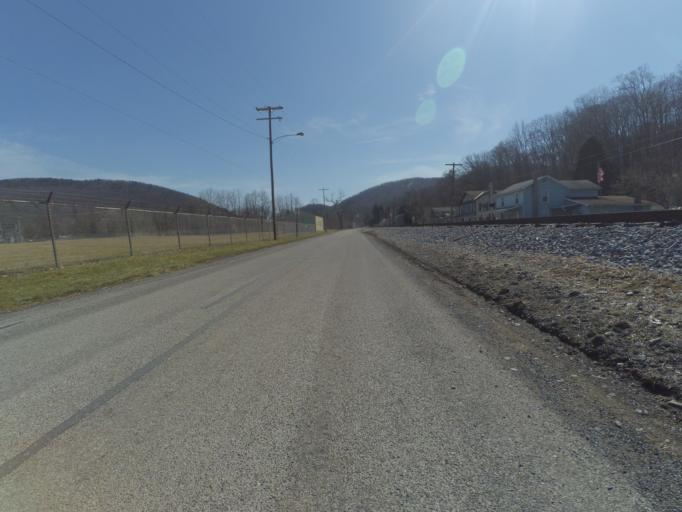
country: US
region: Pennsylvania
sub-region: Centre County
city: Milesburg
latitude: 40.9407
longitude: -77.7904
